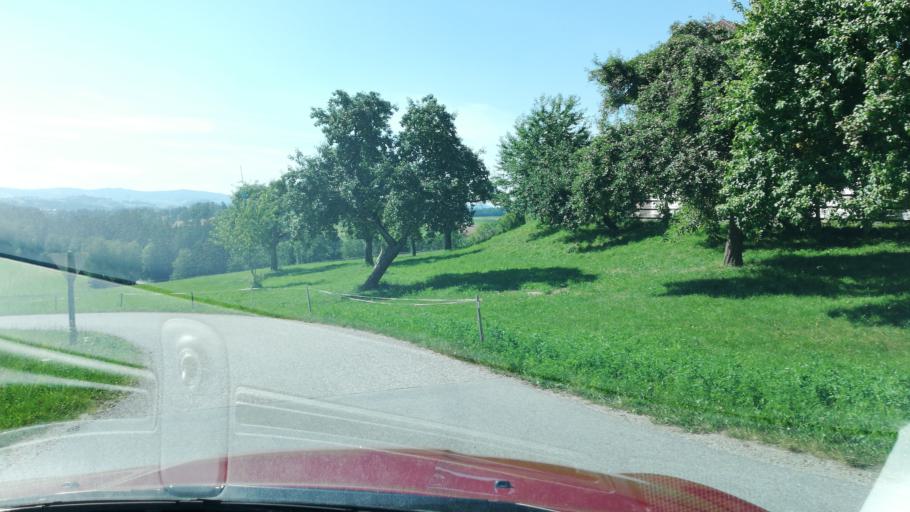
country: AT
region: Upper Austria
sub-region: Politischer Bezirk Rohrbach
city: Kleinzell im Muehlkreis
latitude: 48.4850
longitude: 14.0504
